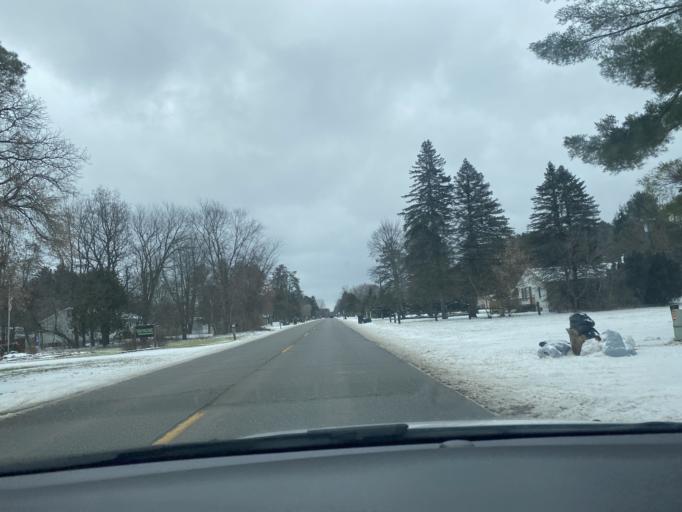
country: US
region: Michigan
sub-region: Lapeer County
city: Barnes Lake-Millers Lake
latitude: 43.2048
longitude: -83.3082
